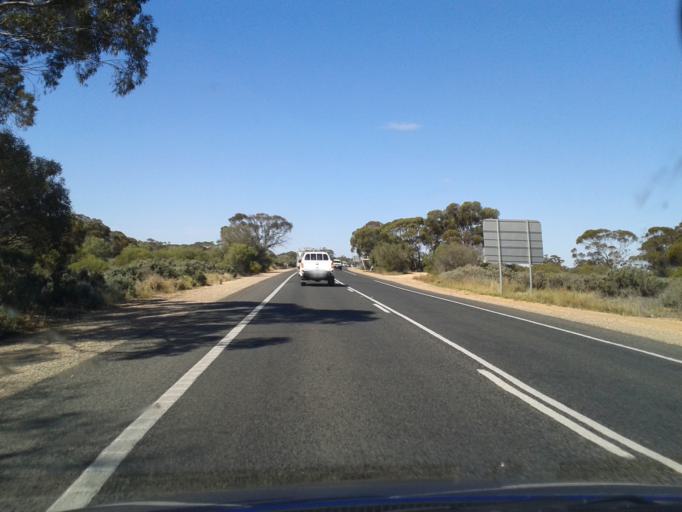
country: AU
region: South Australia
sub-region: Berri and Barmera
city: Berri
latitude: -34.2413
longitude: 140.6291
